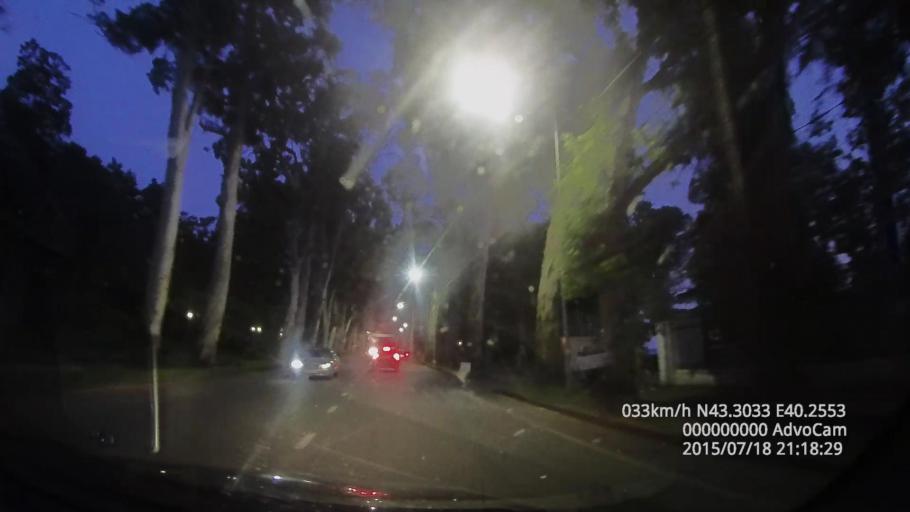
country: GE
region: Abkhazia
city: Gagra
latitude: 43.3031
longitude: 40.2554
